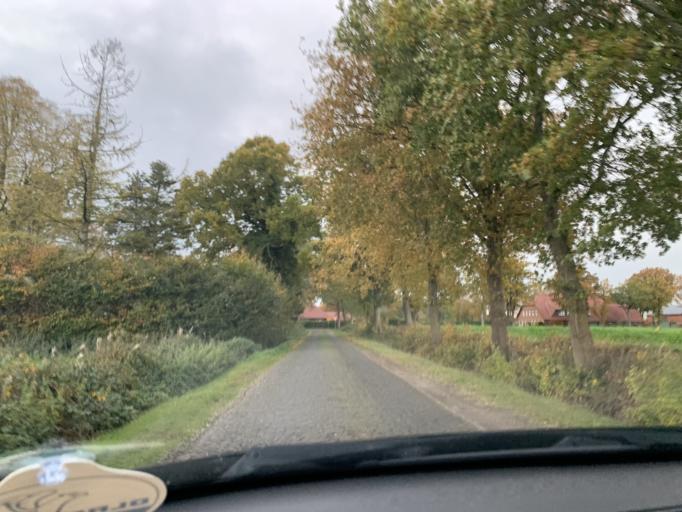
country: DE
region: Lower Saxony
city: Wiefelstede
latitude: 53.2709
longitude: 8.0412
